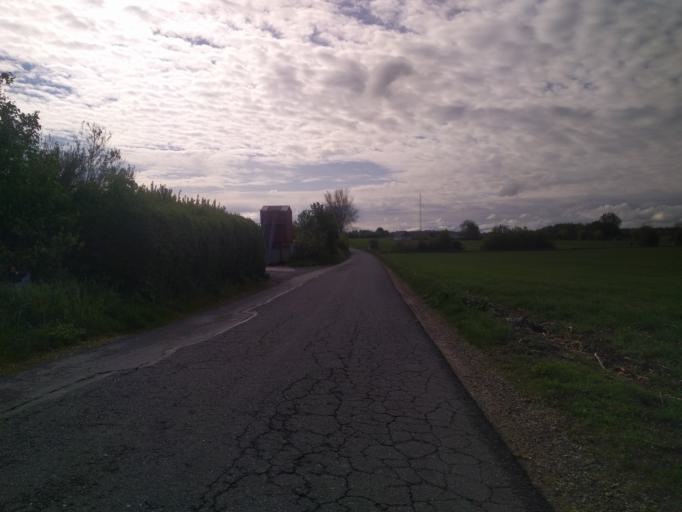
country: DK
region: South Denmark
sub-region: Kerteminde Kommune
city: Kerteminde
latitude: 55.4266
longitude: 10.6347
